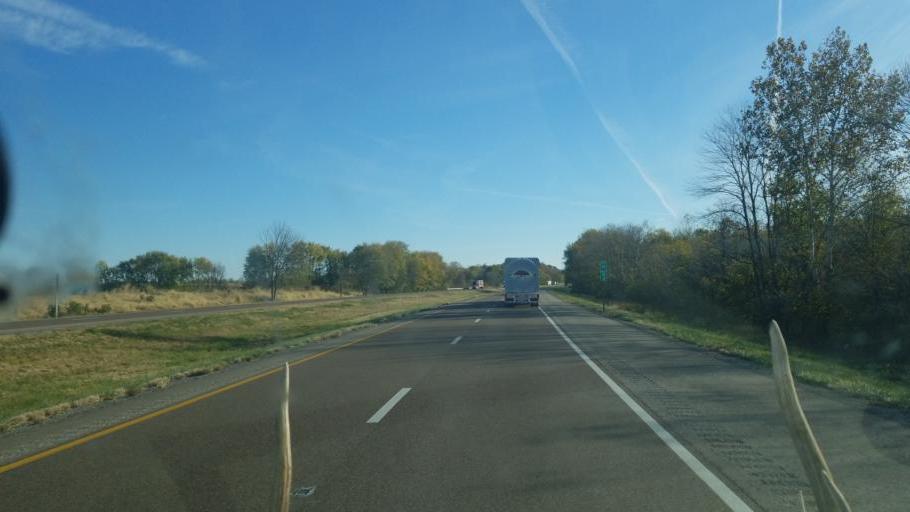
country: US
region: Illinois
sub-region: Madison County
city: Troy
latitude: 38.7603
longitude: -89.8327
